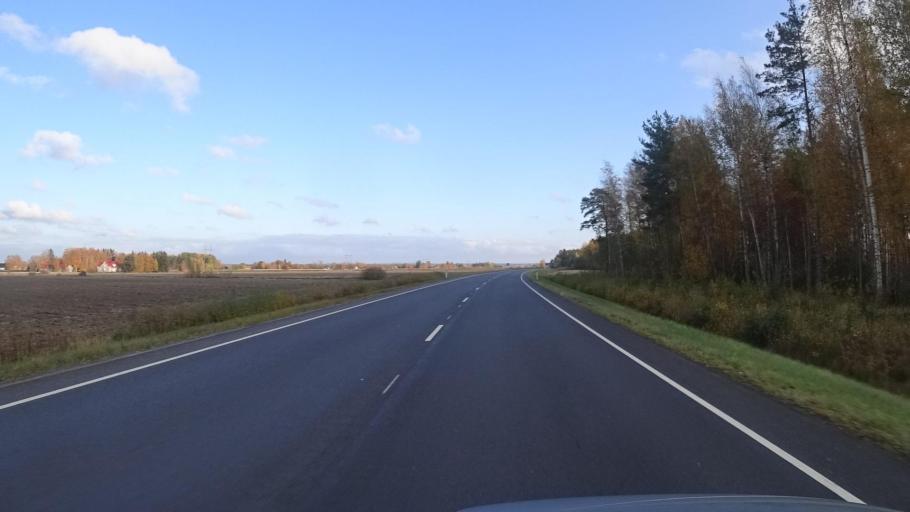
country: FI
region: Satakunta
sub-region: Rauma
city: Saekylae
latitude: 61.0708
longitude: 22.3115
